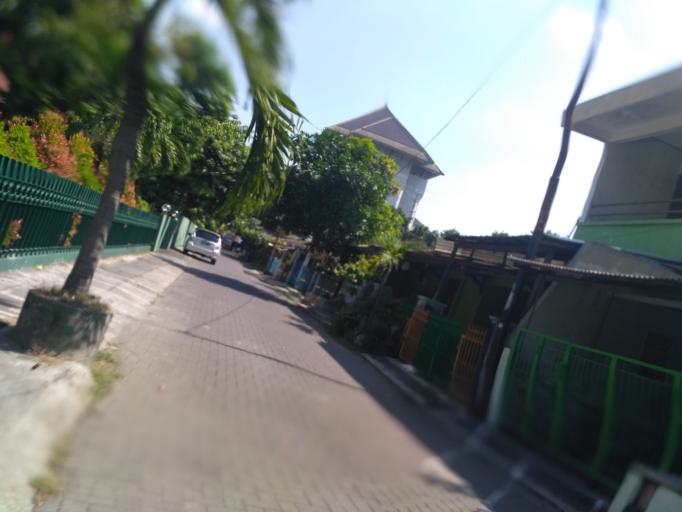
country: ID
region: Central Java
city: Semarang
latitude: -6.9960
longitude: 110.4241
